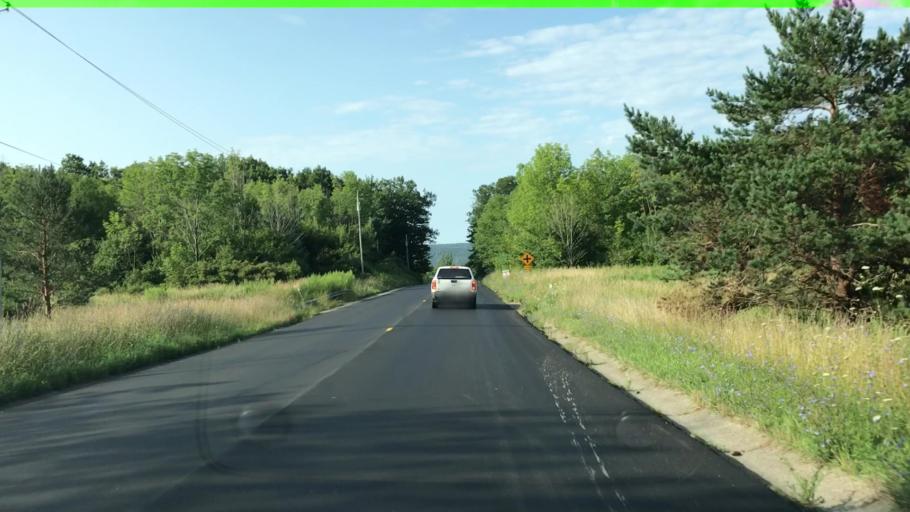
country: US
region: New York
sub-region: Chautauqua County
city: Brocton
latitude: 42.3215
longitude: -79.3456
